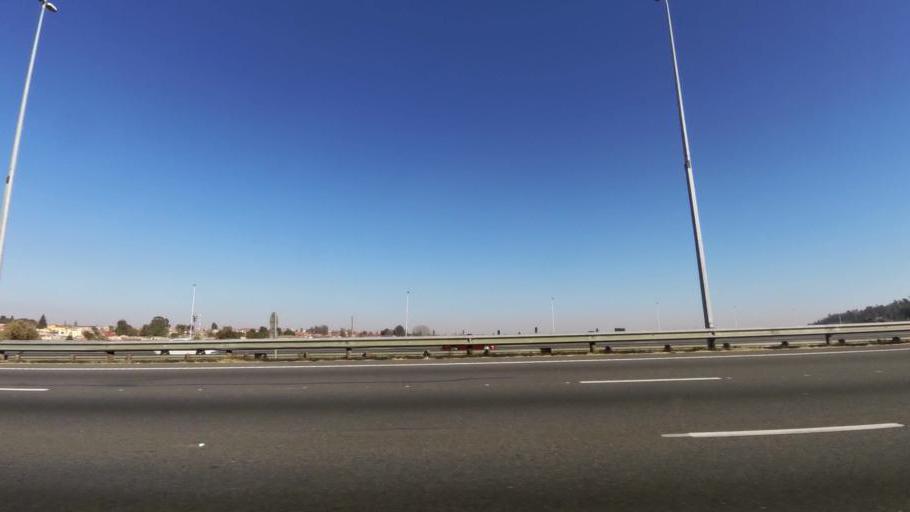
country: ZA
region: Gauteng
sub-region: City of Johannesburg Metropolitan Municipality
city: Johannesburg
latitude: -26.2360
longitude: 27.9607
